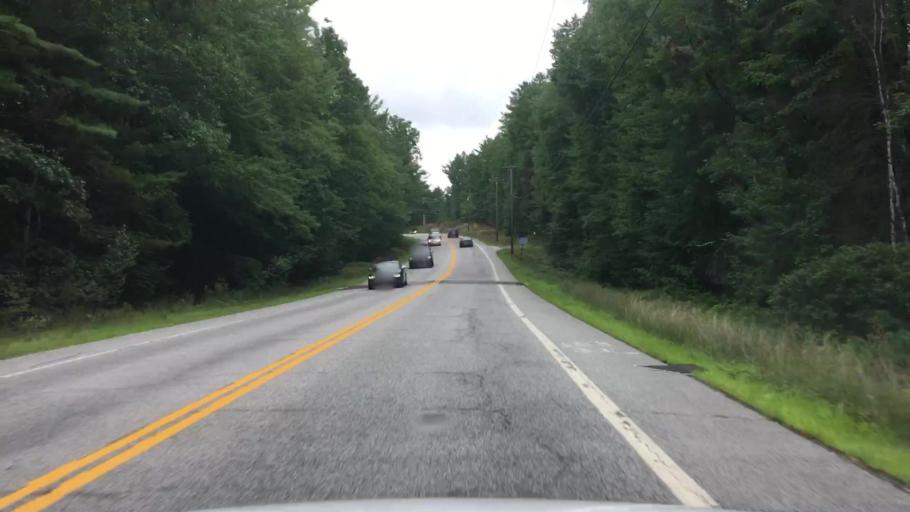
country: US
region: Maine
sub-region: Oxford County
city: Hiram
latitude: 43.8568
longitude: -70.7904
